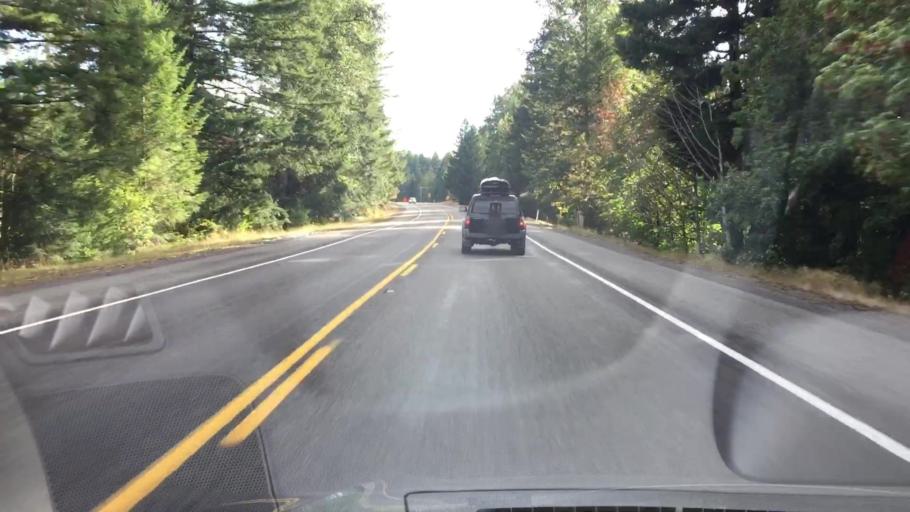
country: US
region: Washington
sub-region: Lewis County
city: Morton
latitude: 46.6228
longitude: -121.6593
